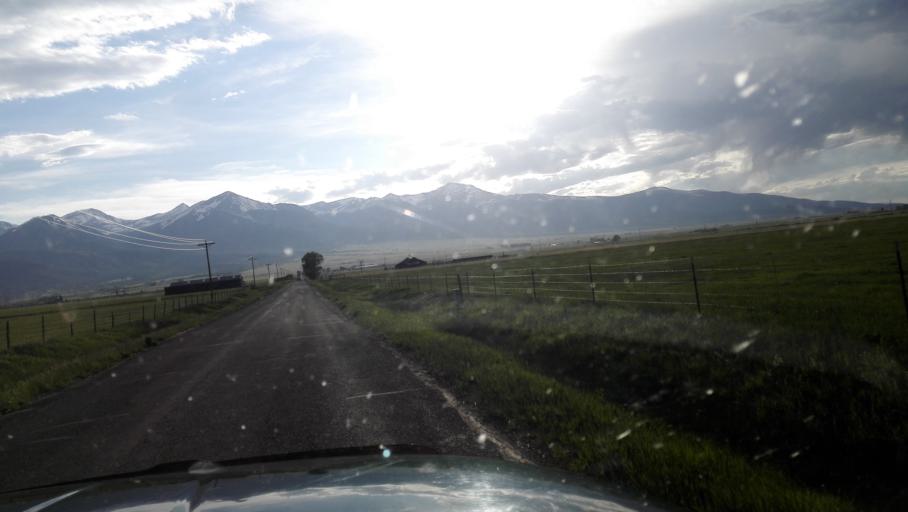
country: US
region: Colorado
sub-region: Custer County
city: Westcliffe
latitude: 38.1317
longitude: -105.4934
